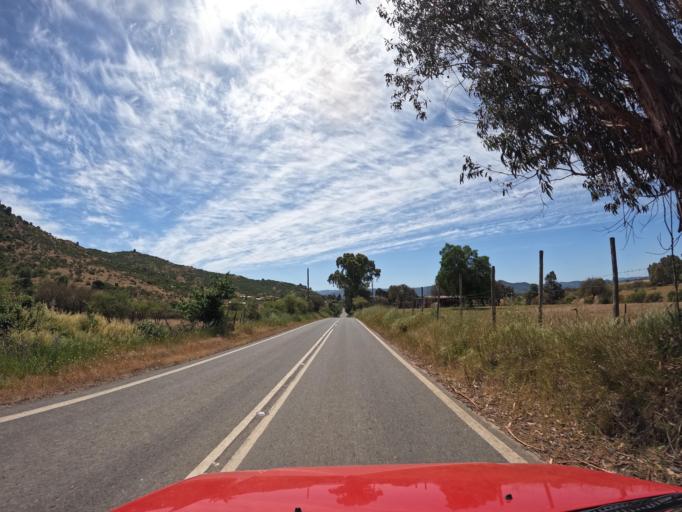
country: CL
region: Maule
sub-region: Provincia de Talca
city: Talca
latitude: -35.0500
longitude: -71.7498
